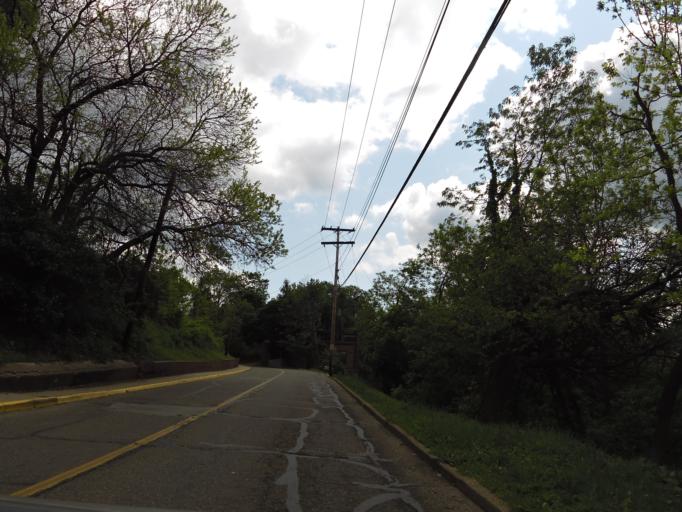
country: US
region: Ohio
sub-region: Athens County
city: Athens
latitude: 39.3324
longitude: -82.1085
